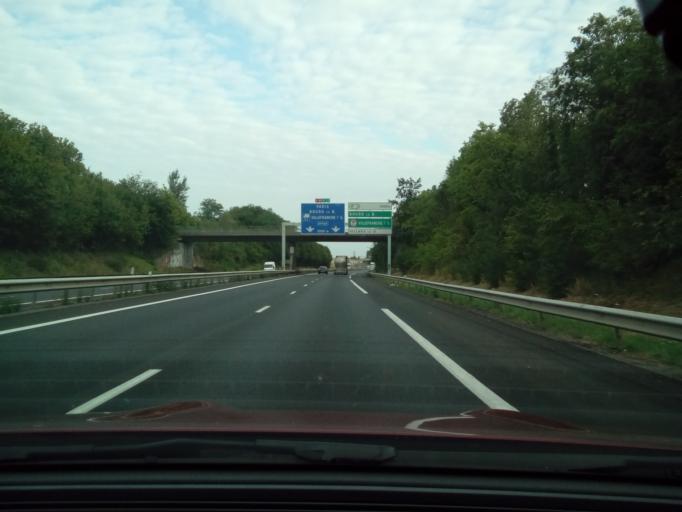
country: FR
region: Rhone-Alpes
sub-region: Departement du Rhone
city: Rillieux-la-Pape
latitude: 45.8414
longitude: 4.9156
